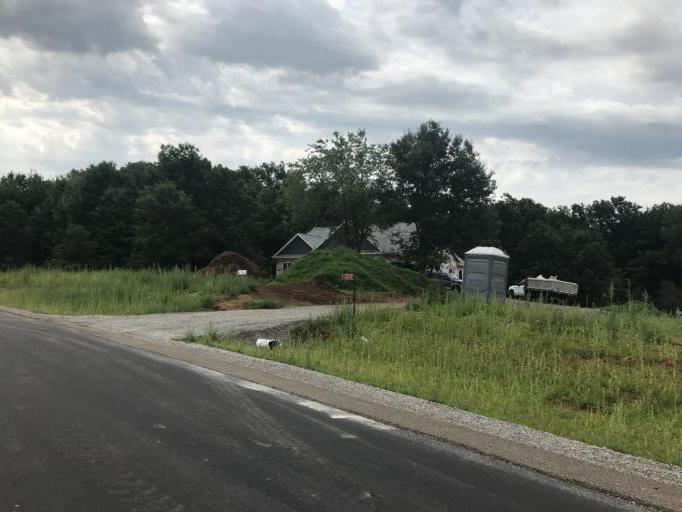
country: US
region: Wisconsin
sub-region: Brown County
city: Suamico
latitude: 44.6851
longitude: -88.0966
